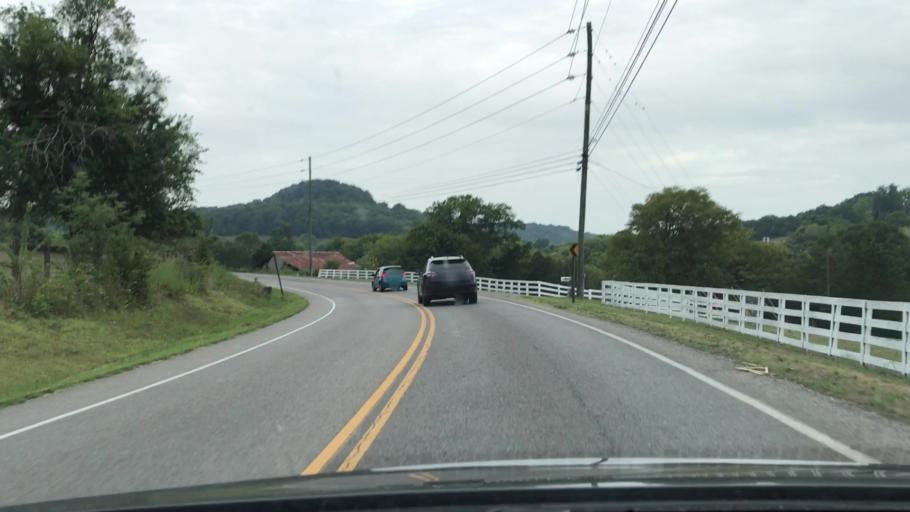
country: US
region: Tennessee
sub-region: Williamson County
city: Nolensville
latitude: 35.9375
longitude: -86.7099
